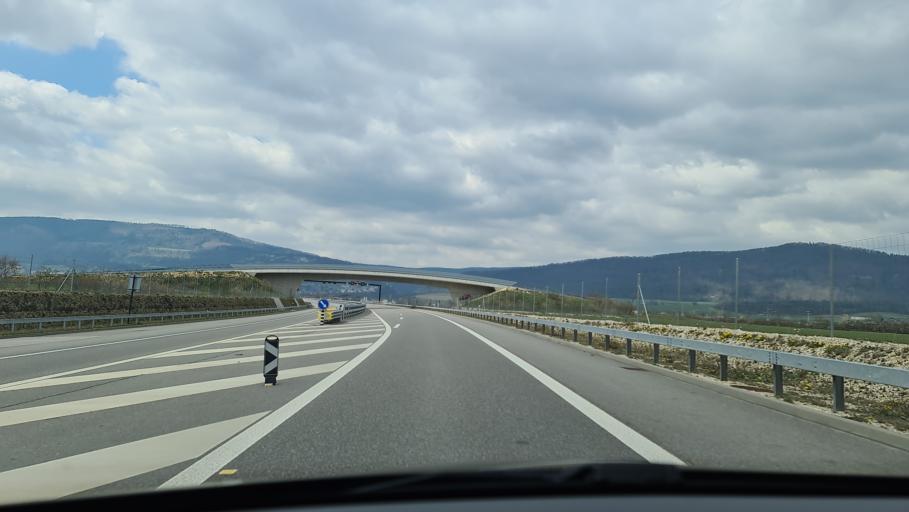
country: CH
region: Jura
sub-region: Delemont District
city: Courrendlin
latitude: 47.3459
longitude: 7.3815
